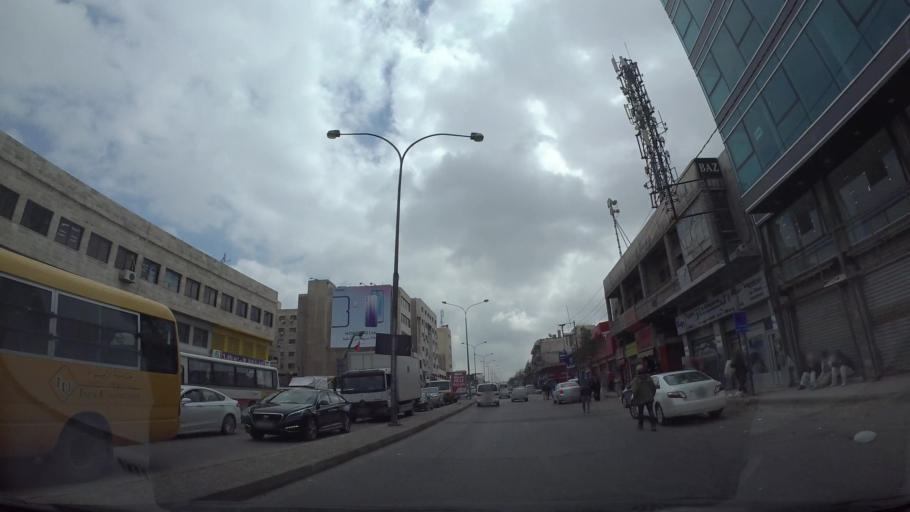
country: JO
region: Amman
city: Al Quwaysimah
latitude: 31.9206
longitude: 35.9383
